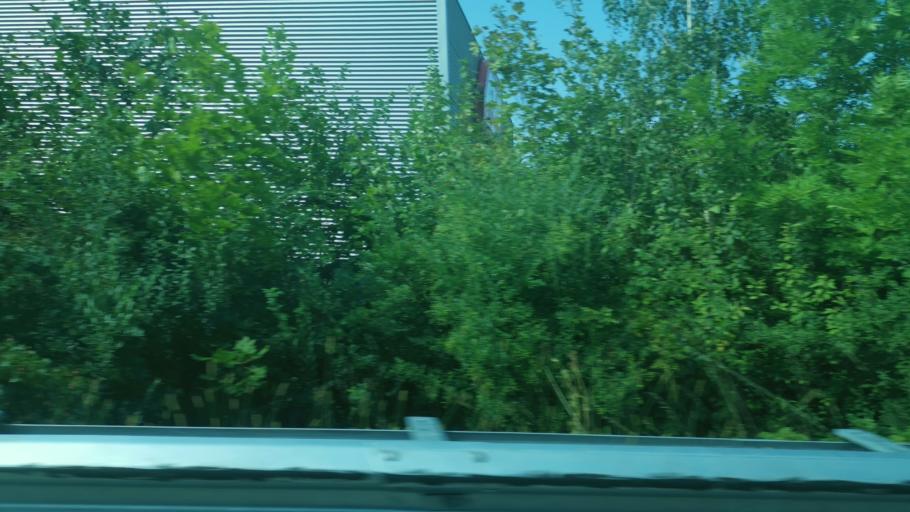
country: DE
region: Bavaria
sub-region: Upper Palatinate
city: Cham
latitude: 49.2291
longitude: 12.6747
